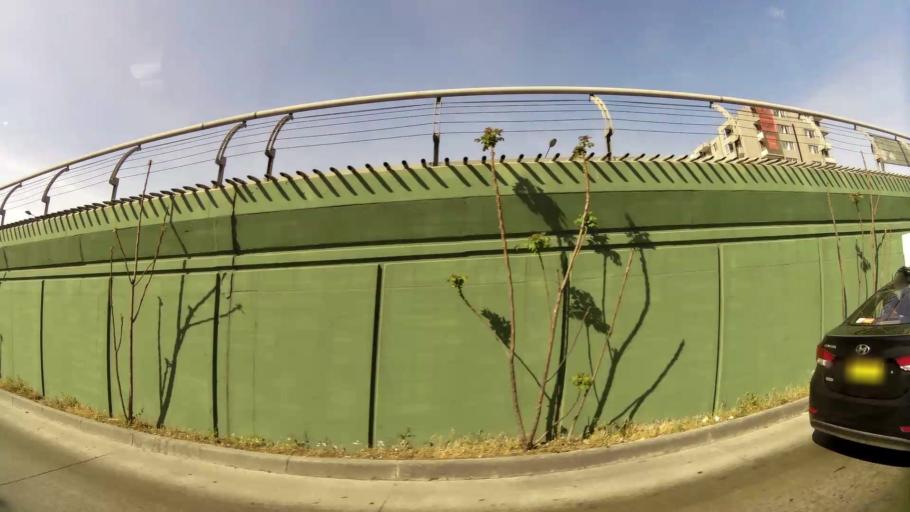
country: CL
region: Santiago Metropolitan
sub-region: Provincia de Santiago
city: La Pintana
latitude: -33.5329
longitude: -70.5943
